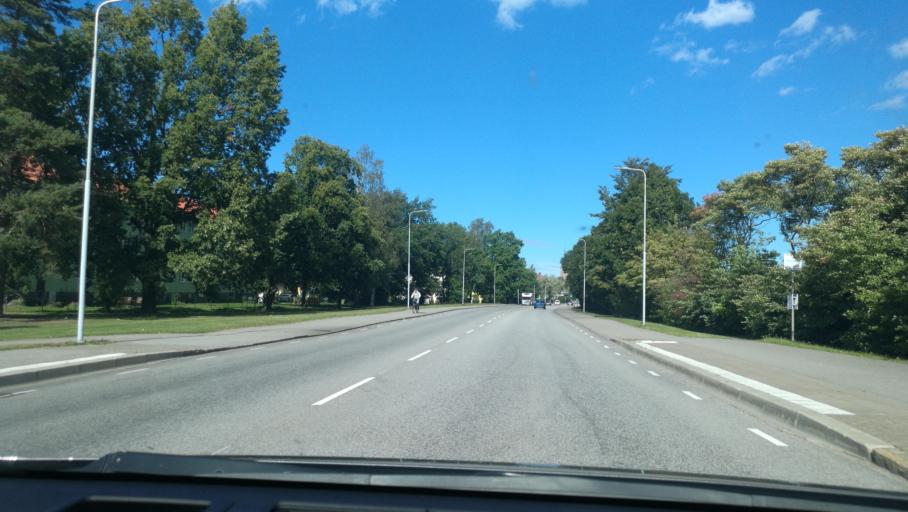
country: SE
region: Vaestra Goetaland
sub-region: Mariestads Kommun
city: Mariestad
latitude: 58.7015
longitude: 13.8203
